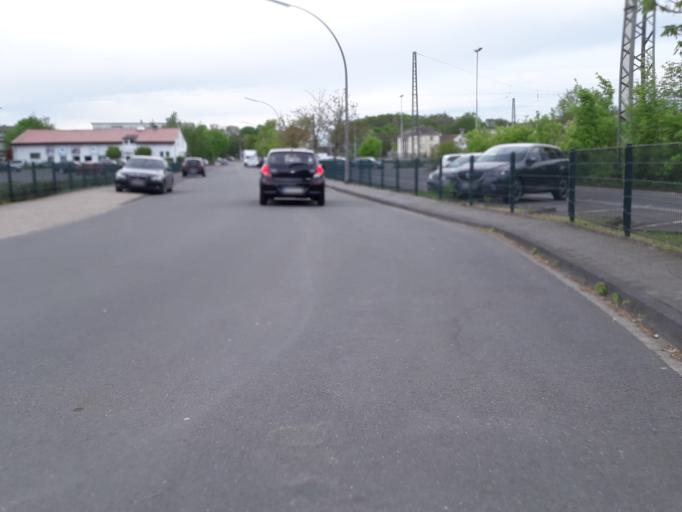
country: DE
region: North Rhine-Westphalia
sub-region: Regierungsbezirk Munster
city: Muenster
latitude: 51.9019
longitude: 7.6551
